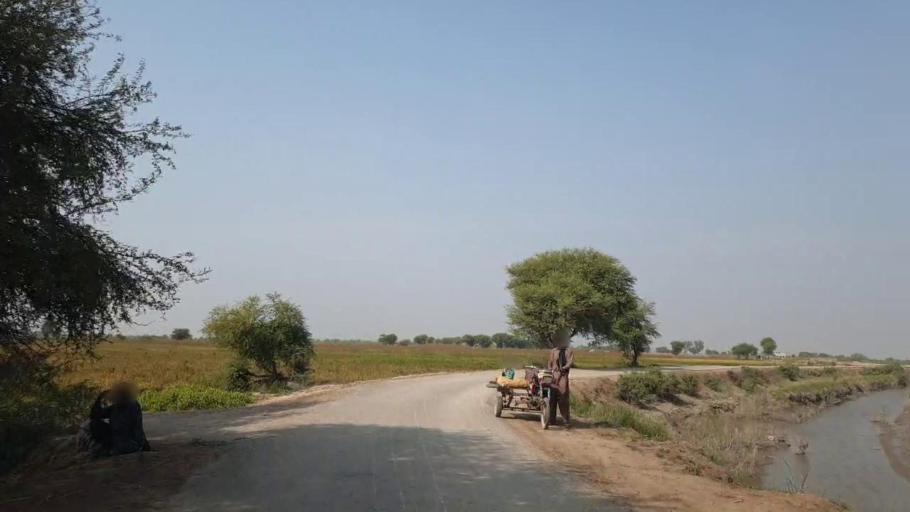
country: PK
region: Sindh
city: Matli
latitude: 24.9502
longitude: 68.5274
